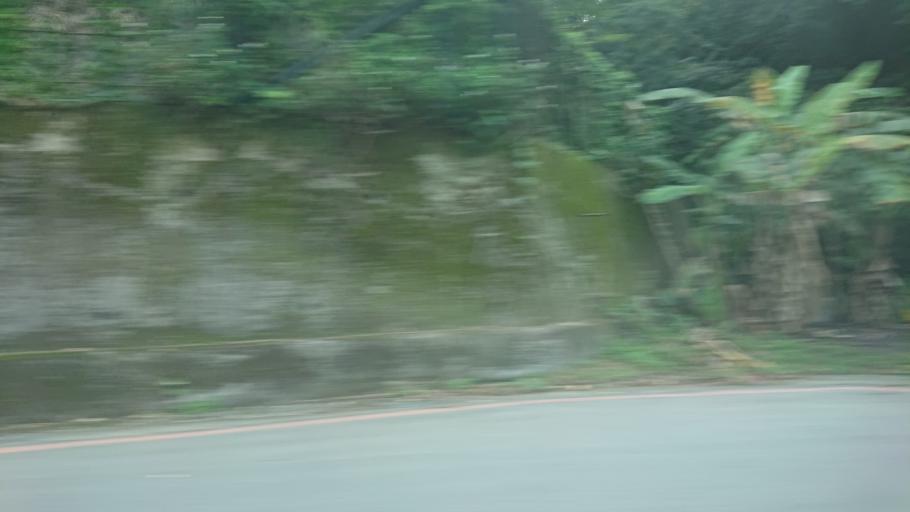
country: TW
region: Taiwan
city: Daxi
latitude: 24.8739
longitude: 121.3867
